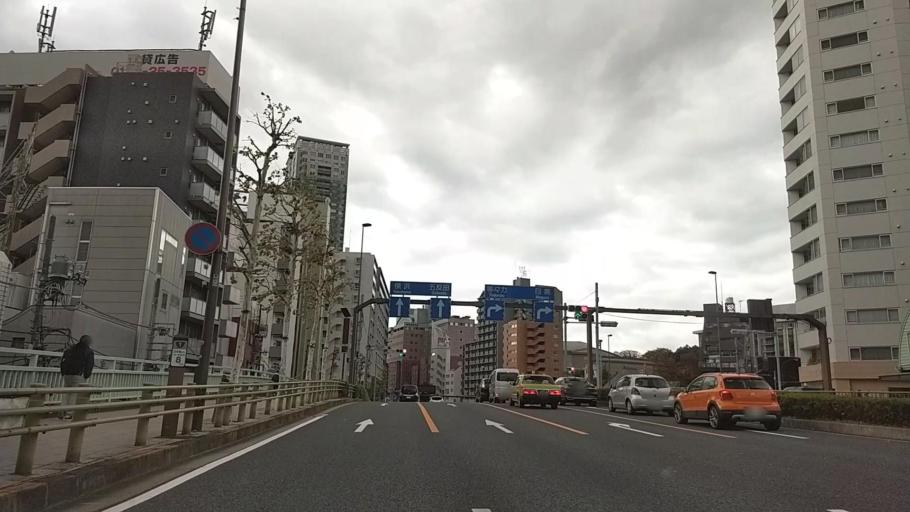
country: JP
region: Tokyo
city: Tokyo
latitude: 35.6410
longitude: 139.7332
